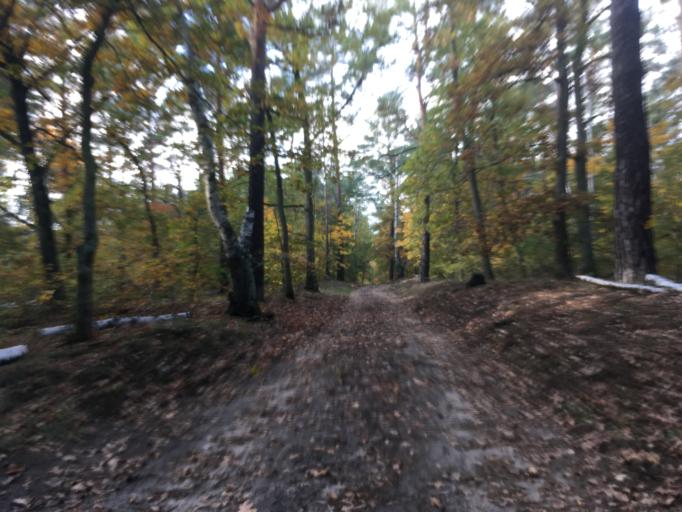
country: DE
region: Berlin
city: Kopenick Bezirk
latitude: 52.4651
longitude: 13.5635
